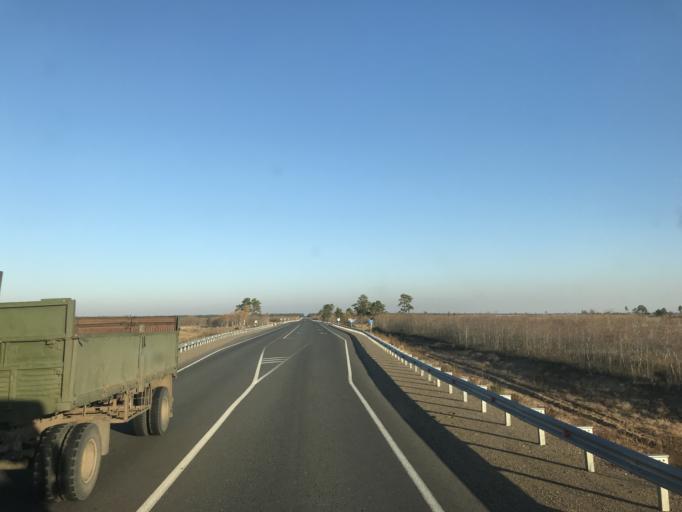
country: KZ
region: Pavlodar
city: Kurchatov
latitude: 51.1033
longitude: 78.9928
